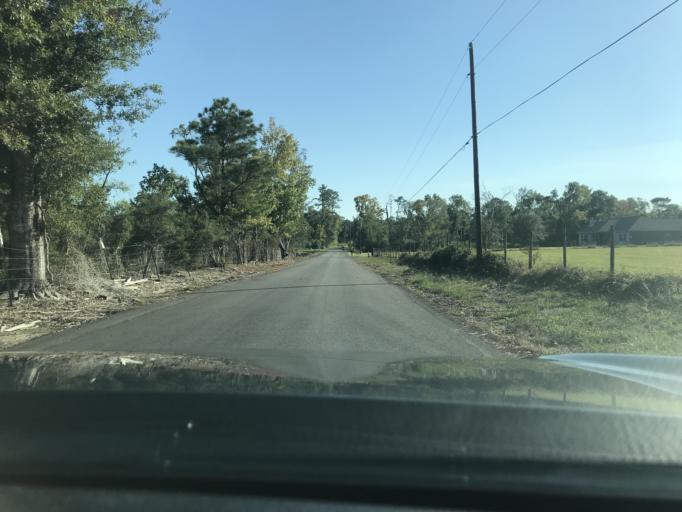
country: US
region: Louisiana
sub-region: Calcasieu Parish
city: Westlake
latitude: 30.3134
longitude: -93.2668
